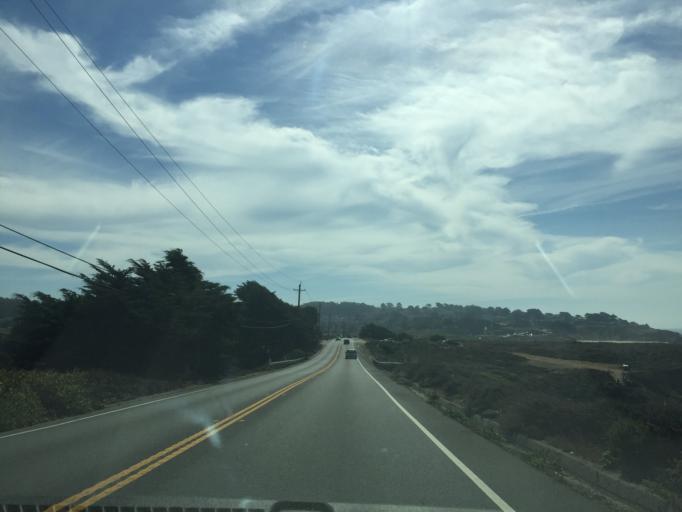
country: US
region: California
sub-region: San Mateo County
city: Montara
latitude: 37.5537
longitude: -122.5125
